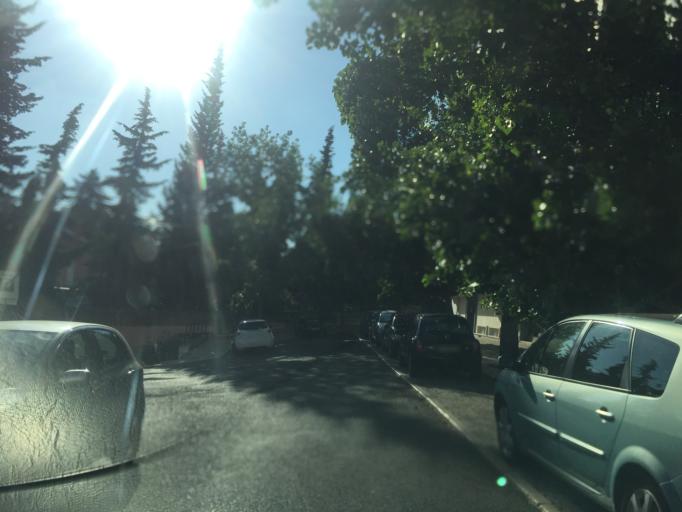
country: PT
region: Lisbon
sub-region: Odivelas
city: Pontinha
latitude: 38.7452
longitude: -9.1798
